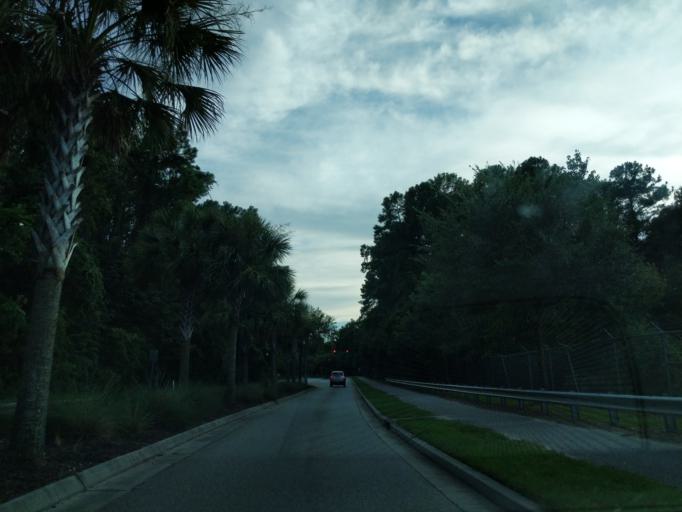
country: US
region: South Carolina
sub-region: Charleston County
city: Isle of Palms
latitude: 32.8339
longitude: -79.8190
